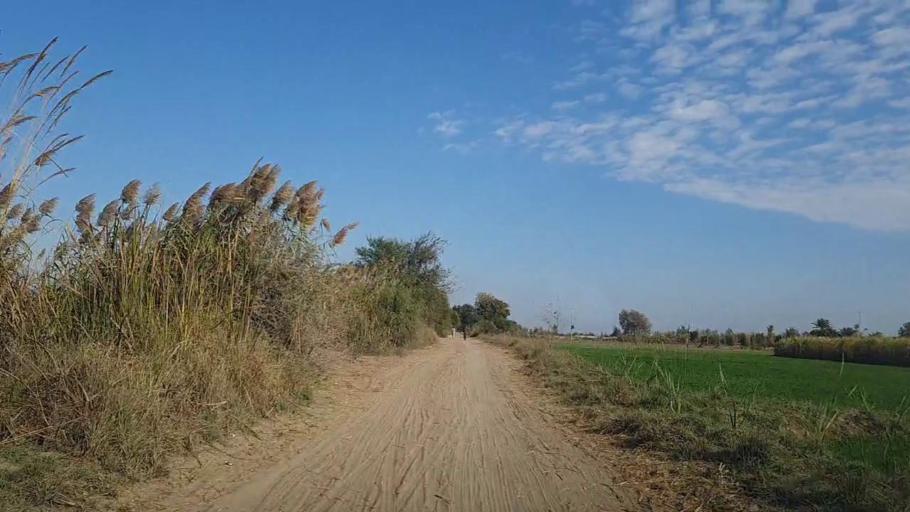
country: PK
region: Sindh
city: Khadro
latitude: 26.3023
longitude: 68.8250
